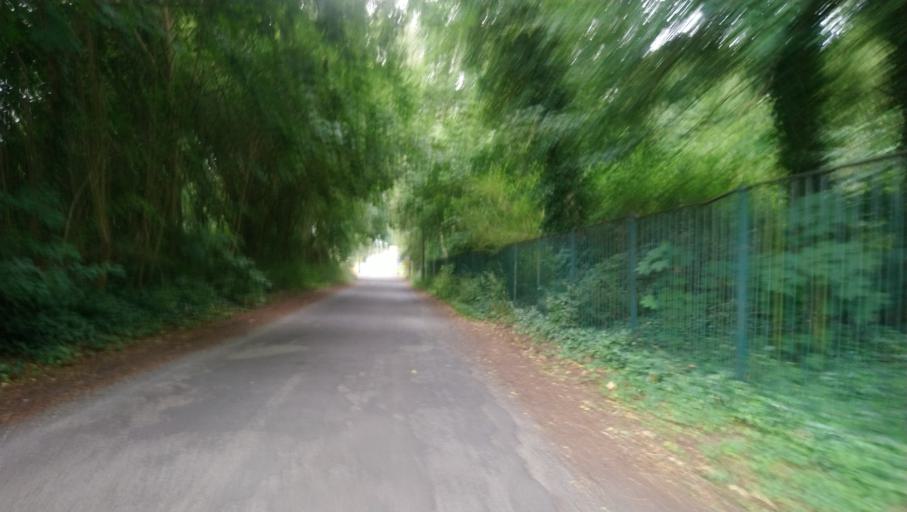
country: DE
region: Mecklenburg-Vorpommern
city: Kritzmow
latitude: 54.0683
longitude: 12.0977
